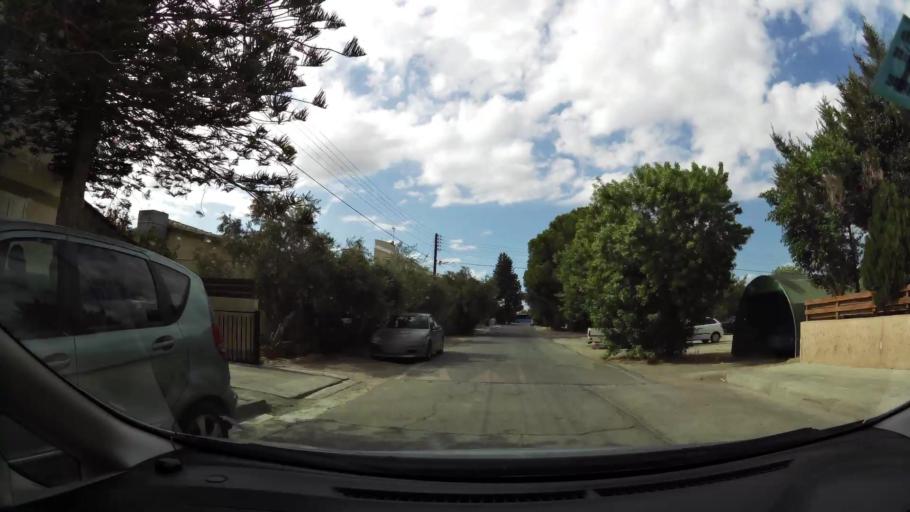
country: CY
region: Lefkosia
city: Nicosia
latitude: 35.1876
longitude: 33.3954
